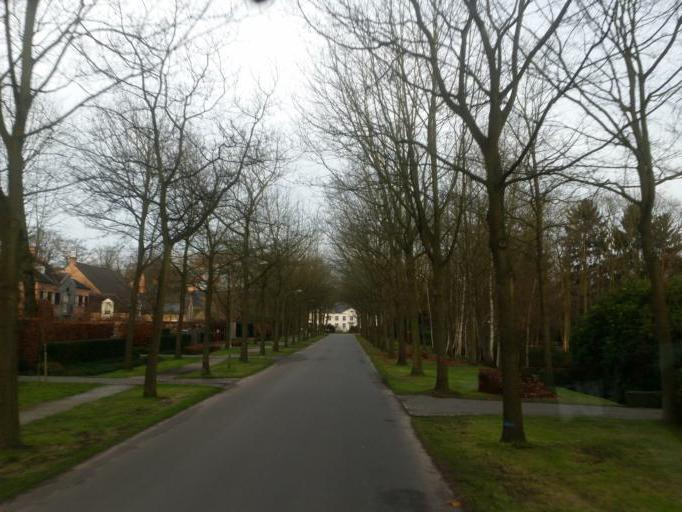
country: BE
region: Flanders
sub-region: Provincie Antwerpen
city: Brasschaat
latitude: 51.3199
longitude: 4.4938
